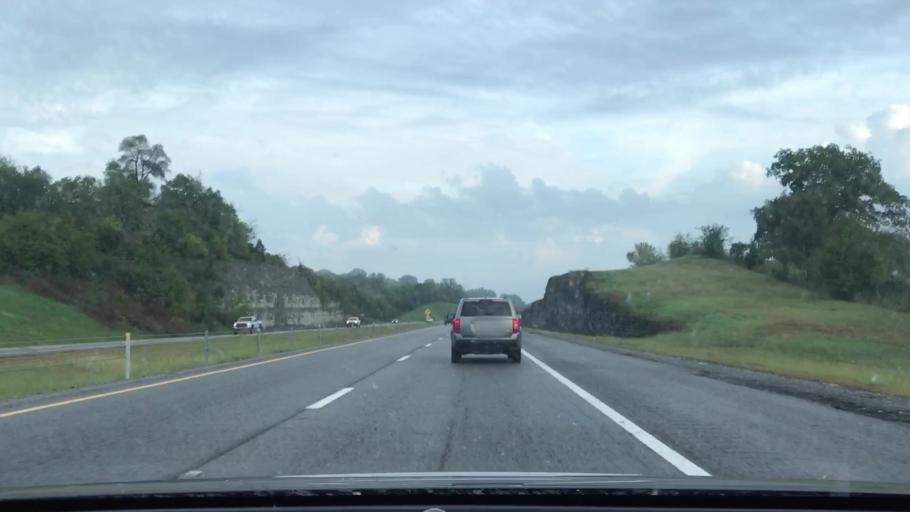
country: US
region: Tennessee
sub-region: Sumner County
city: Shackle Island
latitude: 36.3387
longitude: -86.5494
